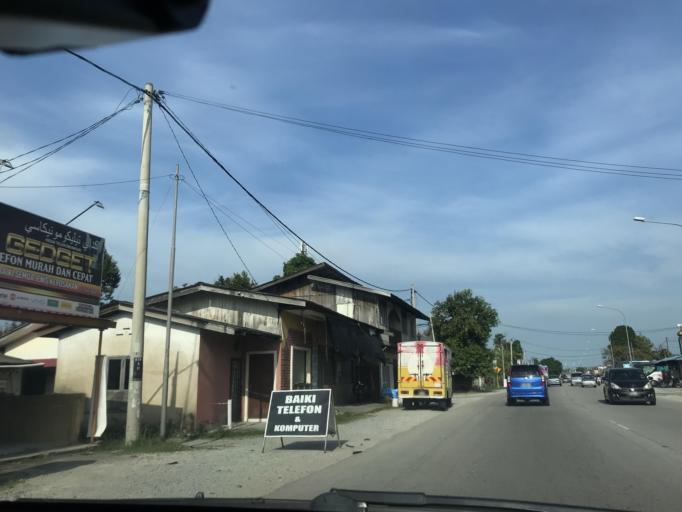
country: MY
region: Kelantan
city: Kota Bharu
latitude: 6.1224
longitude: 102.2827
